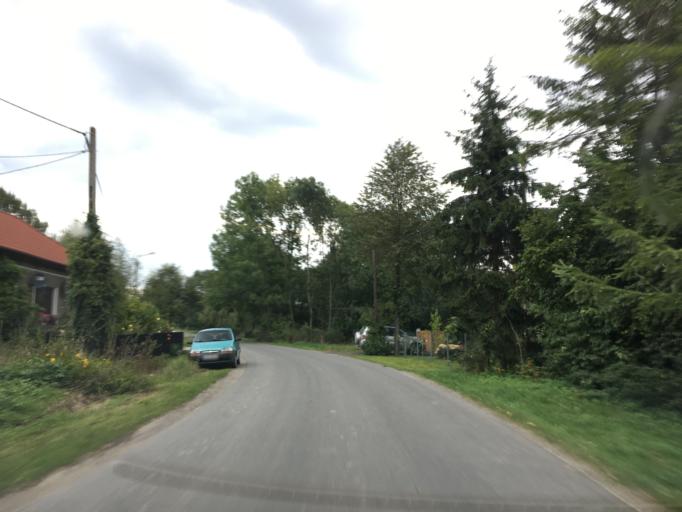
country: PL
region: Lesser Poland Voivodeship
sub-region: Powiat olkuski
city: Wolbrom
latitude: 50.4755
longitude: 19.8140
